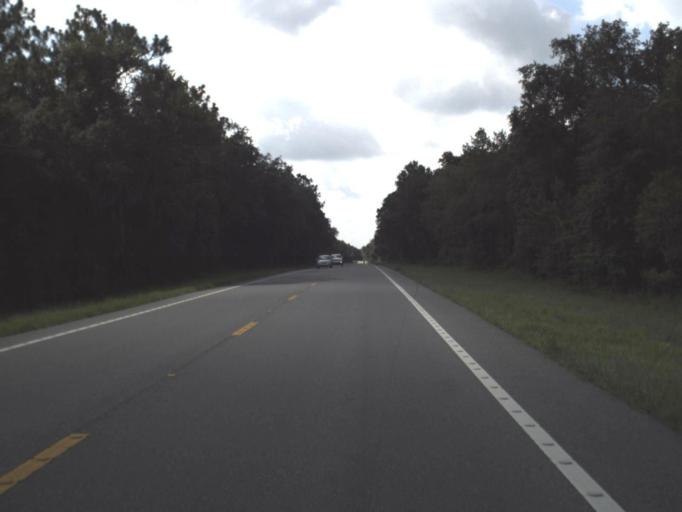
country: US
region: Florida
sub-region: Citrus County
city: Hernando
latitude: 28.9246
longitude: -82.3905
